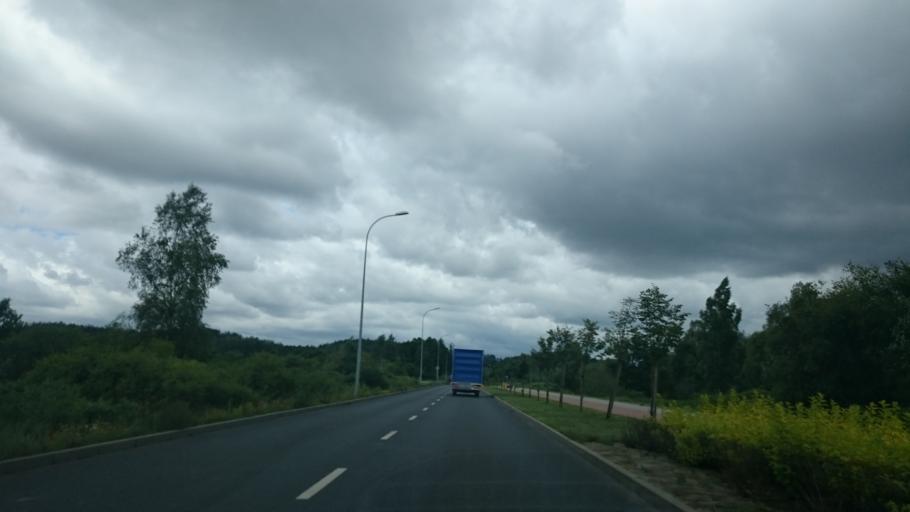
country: PL
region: Kujawsko-Pomorskie
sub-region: Powiat brodnicki
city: Brodnica
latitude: 53.2426
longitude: 19.3779
